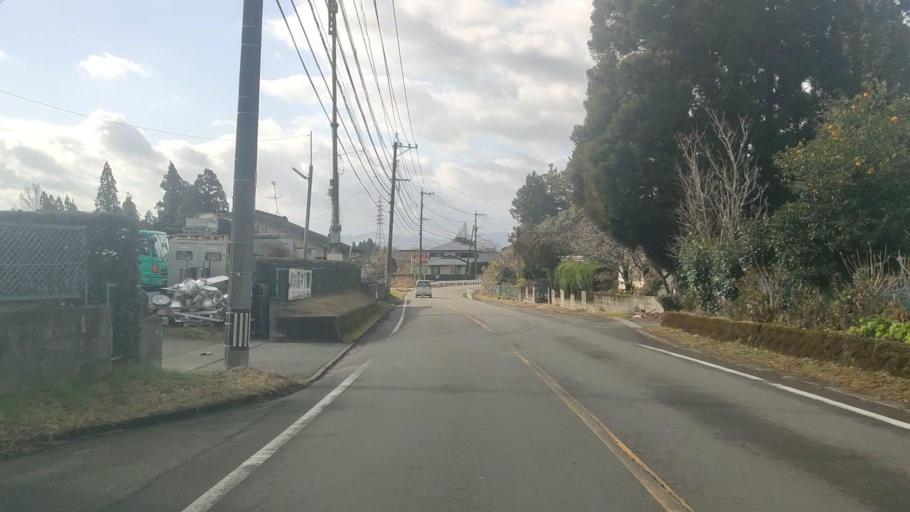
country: JP
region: Kumamoto
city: Hitoyoshi
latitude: 32.2298
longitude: 130.7840
